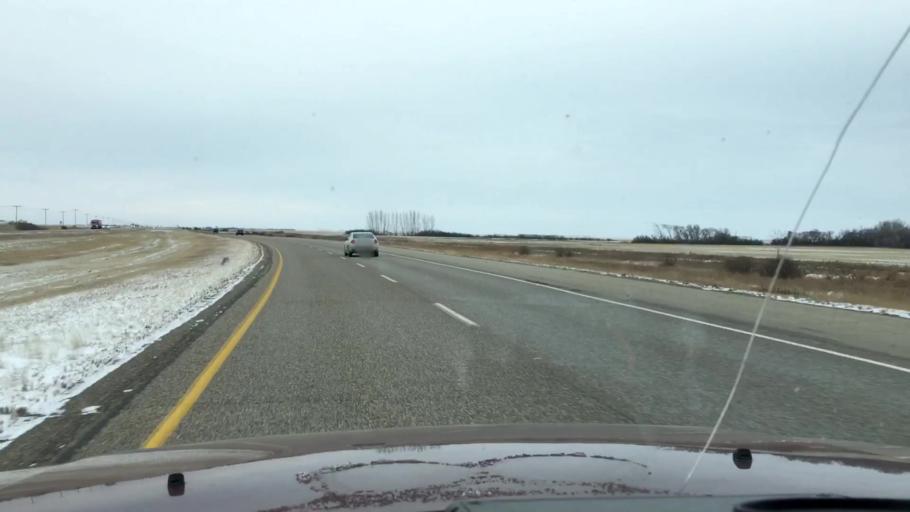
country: CA
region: Saskatchewan
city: Watrous
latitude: 51.1439
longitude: -105.9059
